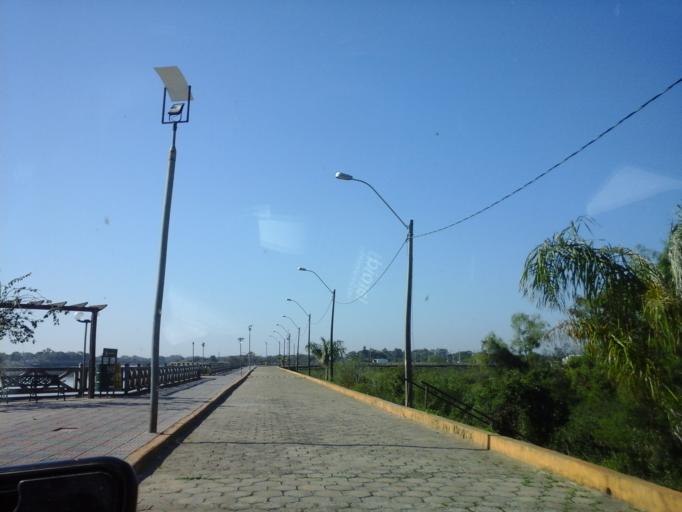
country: PY
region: Neembucu
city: Pilar
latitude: -26.8526
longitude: -58.3047
